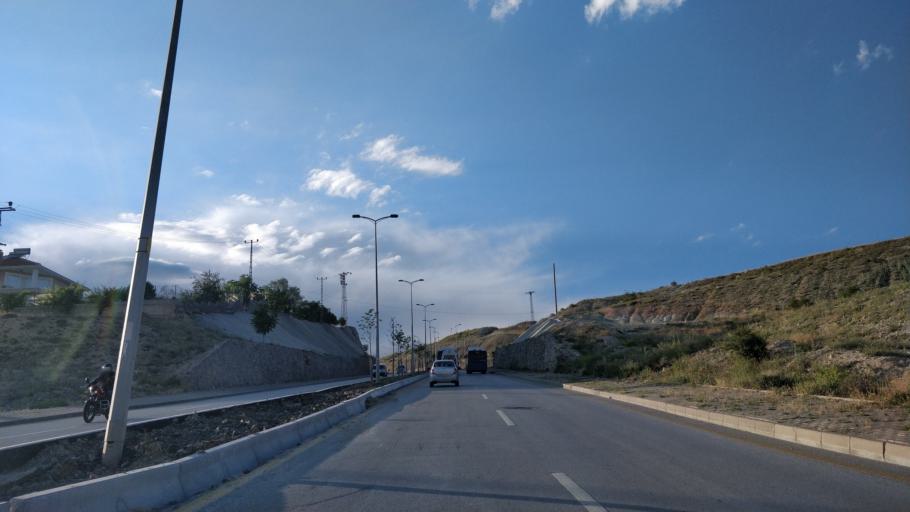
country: TR
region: Ankara
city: Etimesgut
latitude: 39.8299
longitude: 32.5554
